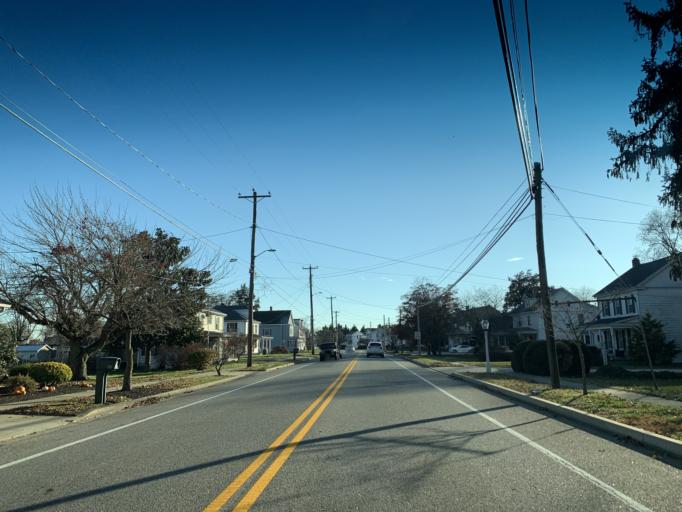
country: US
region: Delaware
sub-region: New Castle County
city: Middletown
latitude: 39.3447
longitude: -75.8792
